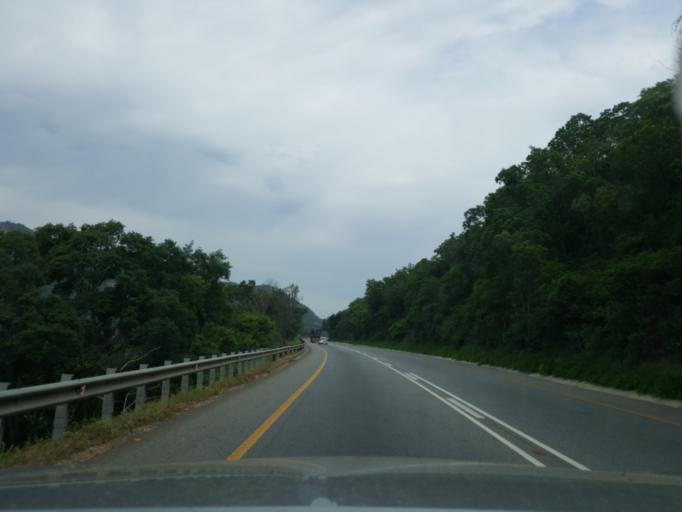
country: ZA
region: Mpumalanga
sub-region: Ehlanzeni District
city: Nelspruit
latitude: -25.5095
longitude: 31.2043
